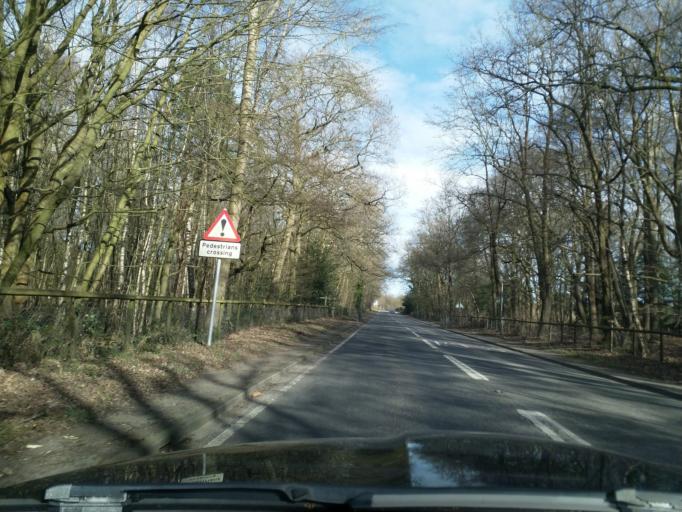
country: GB
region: England
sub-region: Hampshire
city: Aldershot
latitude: 51.2618
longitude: -0.7751
